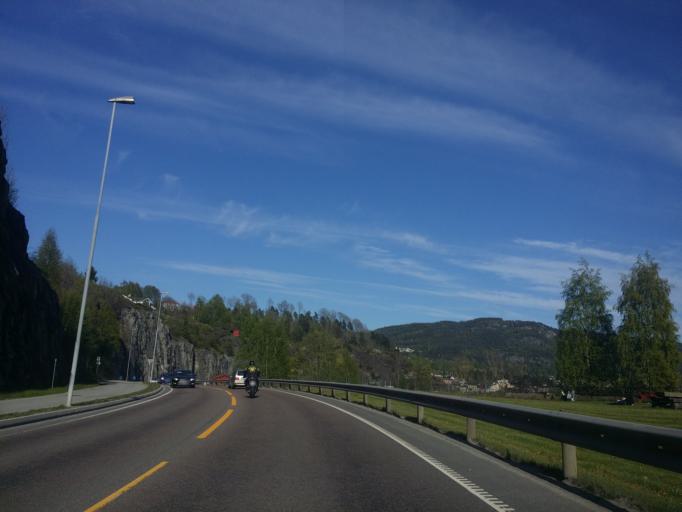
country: NO
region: Telemark
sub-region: Notodden
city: Notodden
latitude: 59.5608
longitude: 9.2402
